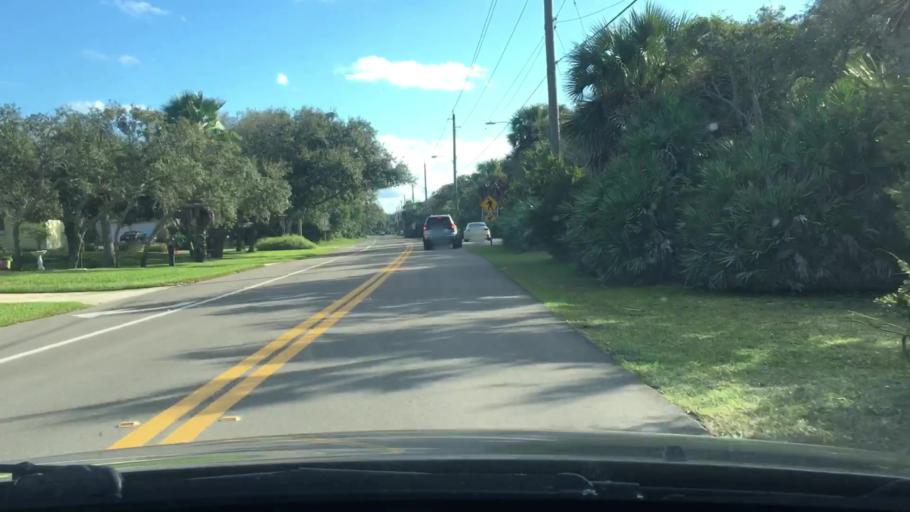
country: US
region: Florida
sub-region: Volusia County
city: Ormond-by-the-Sea
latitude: 29.3822
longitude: -81.0871
